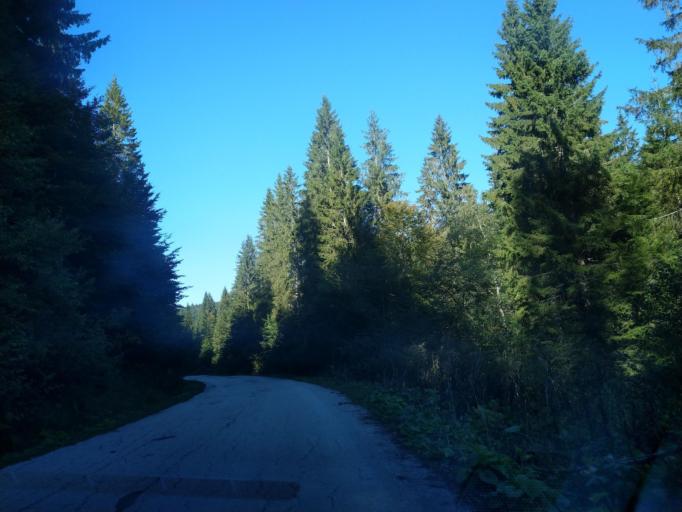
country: RS
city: Sokolovica
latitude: 43.3601
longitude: 20.2565
